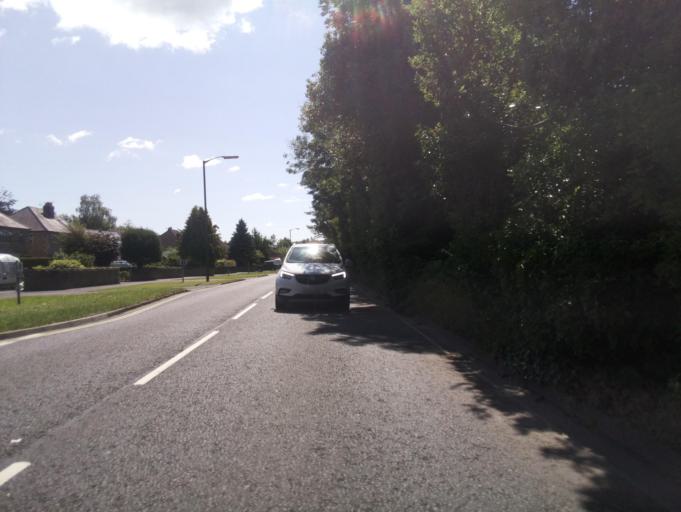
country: GB
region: England
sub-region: Derbyshire
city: Bakewell
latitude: 53.2084
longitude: -1.6703
